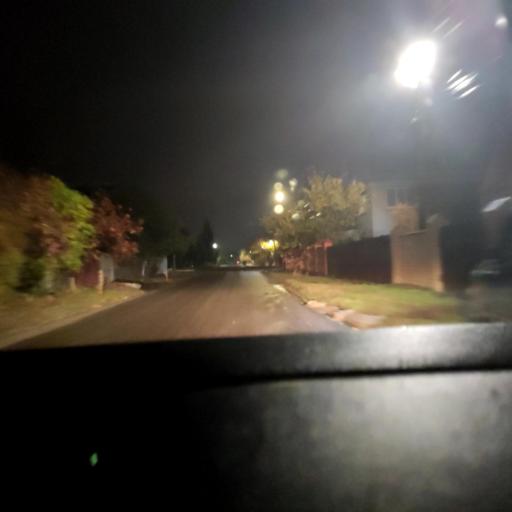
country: RU
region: Voronezj
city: Semiluki
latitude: 51.7070
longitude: 39.0291
